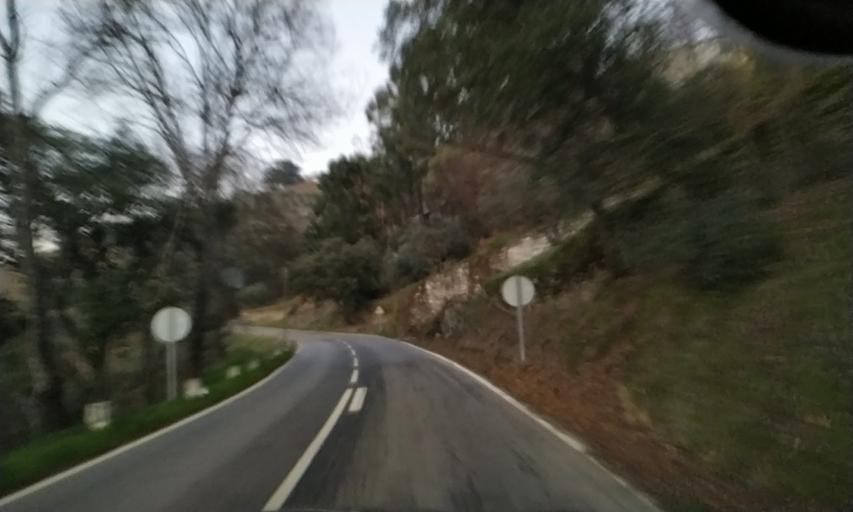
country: PT
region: Vila Real
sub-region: Sabrosa
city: Vilela
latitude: 41.2083
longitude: -7.5413
